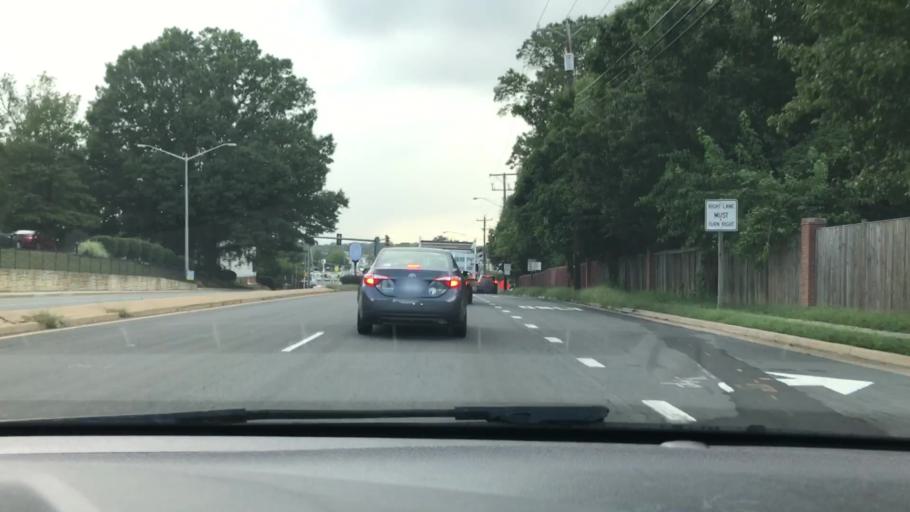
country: US
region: Virginia
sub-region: Fairfax County
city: Annandale
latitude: 38.8350
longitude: -77.1850
